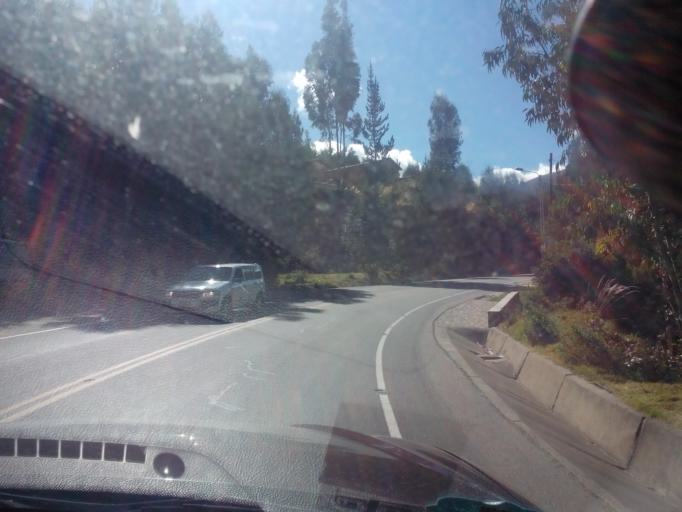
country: PE
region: Cusco
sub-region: Provincia de Quispicanchis
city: Urcos
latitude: -13.6889
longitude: -71.6047
